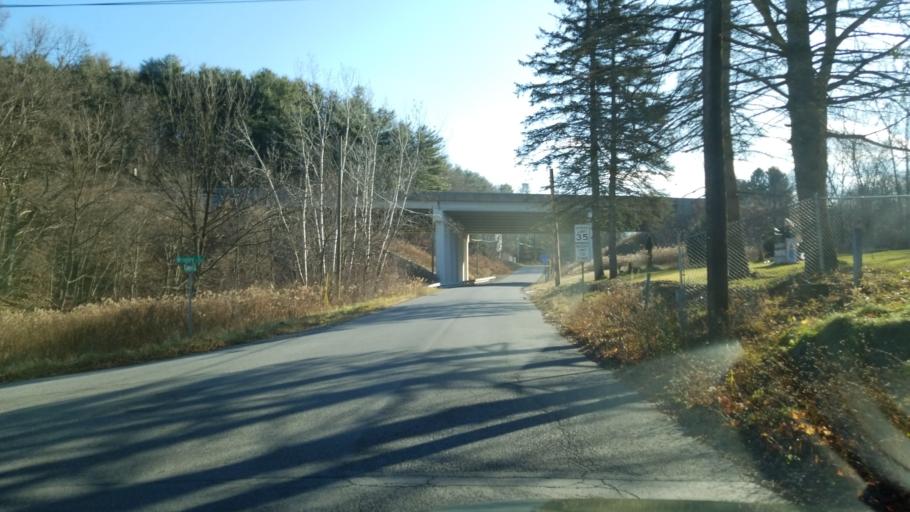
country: US
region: Pennsylvania
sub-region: Clearfield County
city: Clearfield
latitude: 41.0179
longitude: -78.4293
